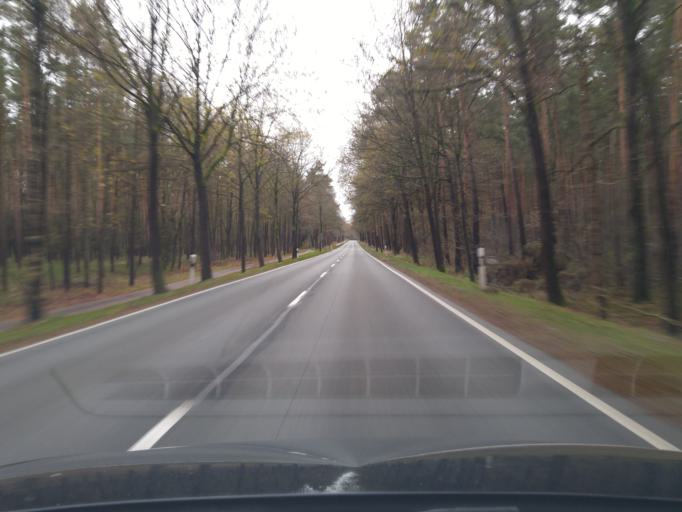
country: DE
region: Lower Saxony
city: Winsen
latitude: 52.7216
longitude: 9.9234
